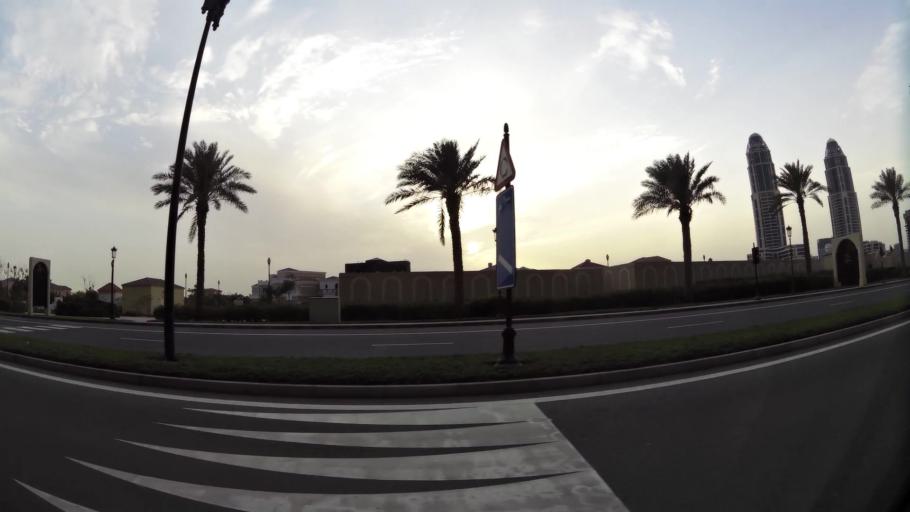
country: QA
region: Baladiyat ad Dawhah
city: Doha
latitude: 25.3683
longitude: 51.5383
